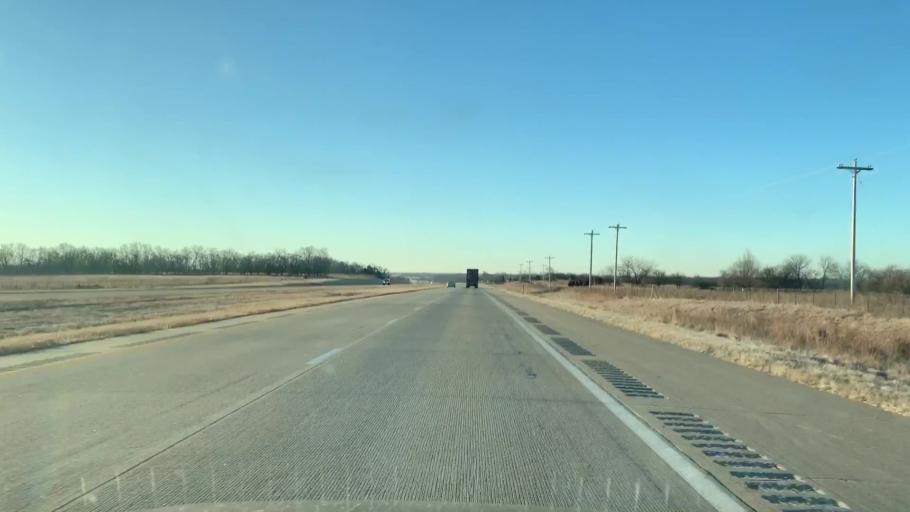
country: US
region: Kansas
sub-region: Linn County
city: Pleasanton
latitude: 38.0911
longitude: -94.7136
